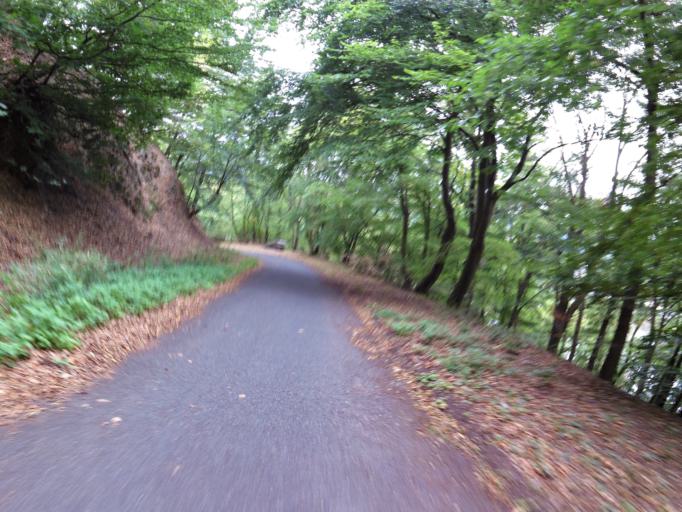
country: DE
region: North Rhine-Westphalia
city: Heimbach
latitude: 50.6190
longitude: 6.3971
